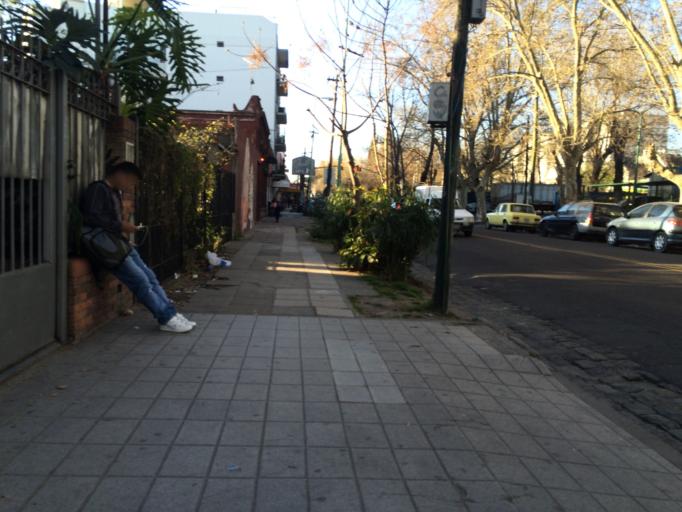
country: AR
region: Buenos Aires
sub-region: Partido de Lomas de Zamora
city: Lomas de Zamora
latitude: -34.7771
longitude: -58.3972
